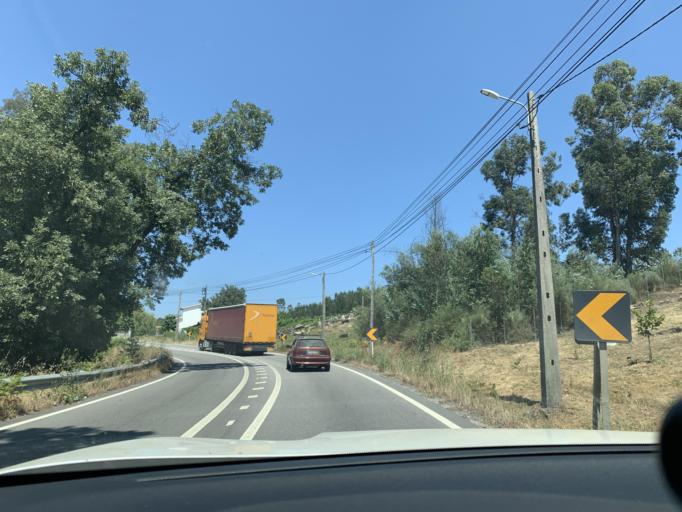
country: PT
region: Viseu
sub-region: Mangualde
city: Mangualde
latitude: 40.5978
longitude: -7.7926
